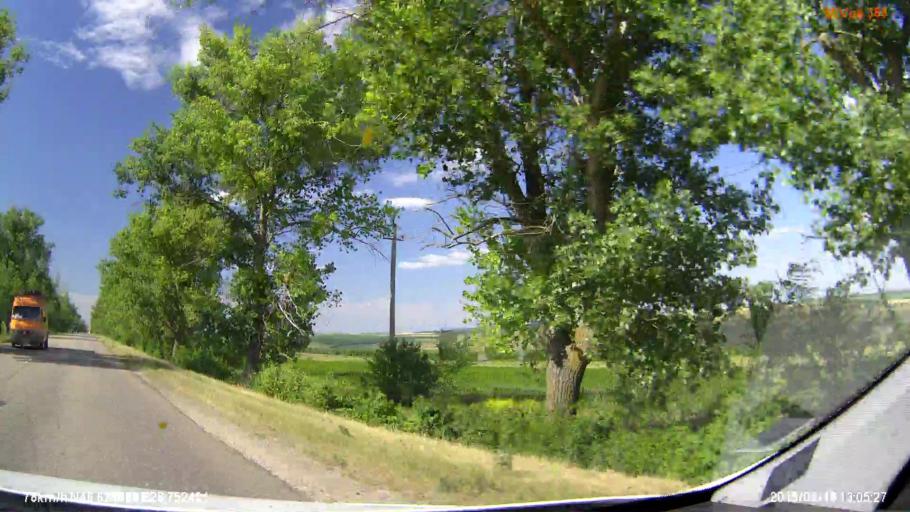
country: MD
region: Cimislia
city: Cimislia
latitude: 46.6249
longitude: 28.7524
